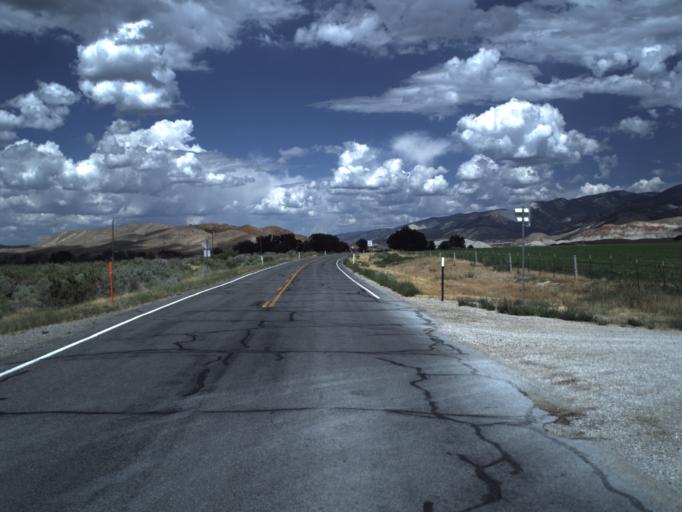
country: US
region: Utah
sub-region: Sanpete County
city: Centerfield
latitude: 39.1380
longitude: -111.7717
